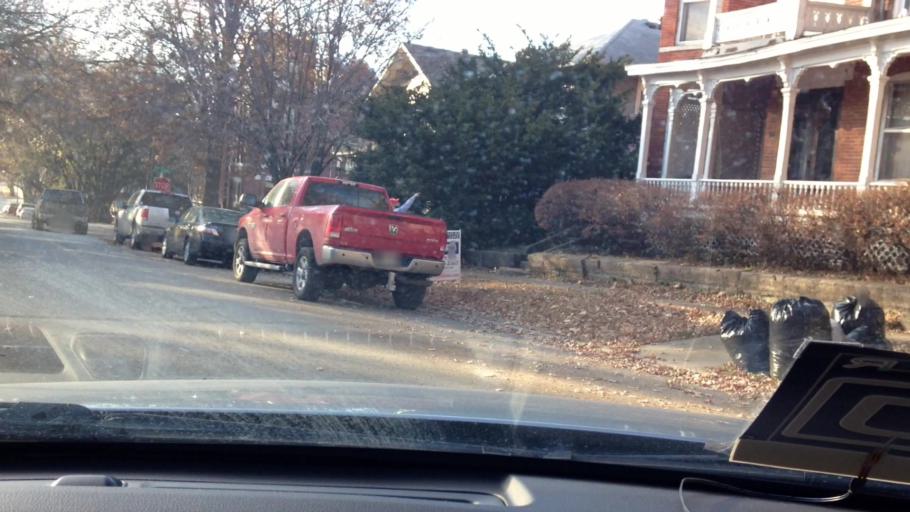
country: US
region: Kansas
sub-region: Leavenworth County
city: Leavenworth
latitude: 39.3204
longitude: -94.9183
